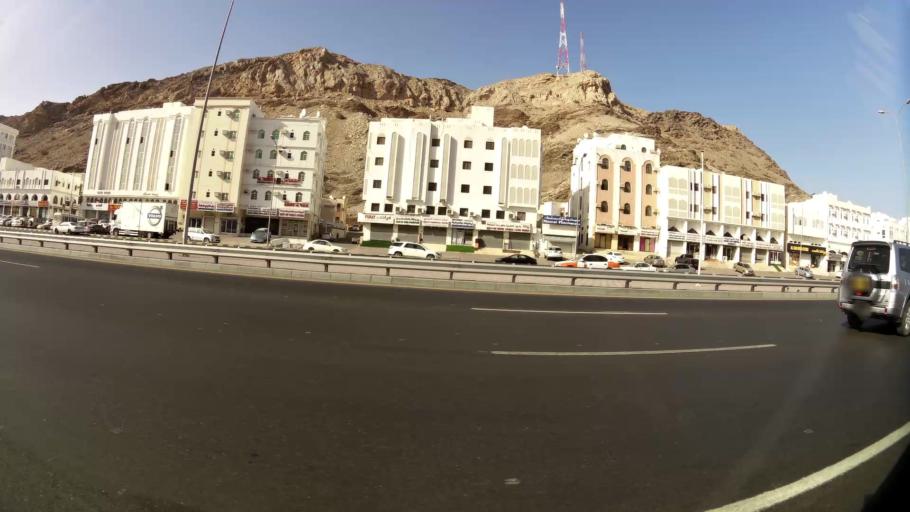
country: OM
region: Muhafazat Masqat
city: Muscat
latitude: 23.5899
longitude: 58.5317
